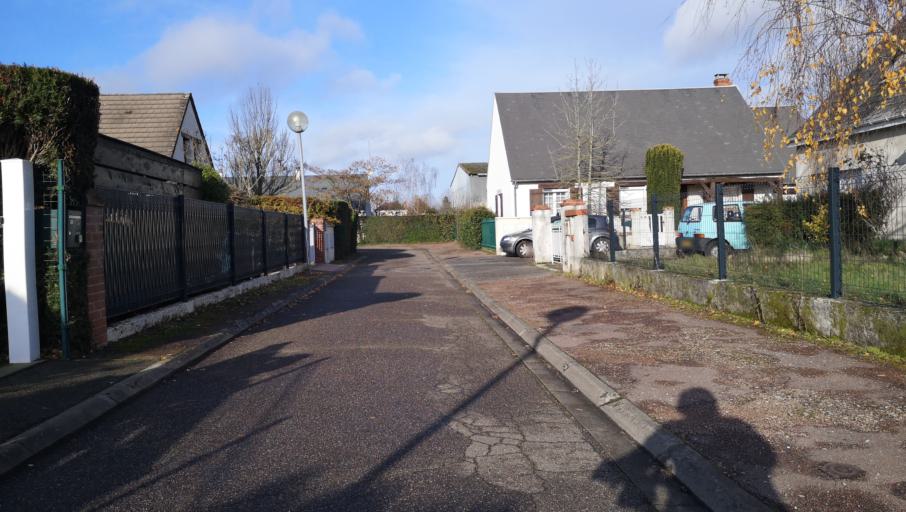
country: FR
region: Centre
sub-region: Departement du Loiret
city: Saint-Pryve-Saint-Mesmin
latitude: 47.8800
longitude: 1.8727
